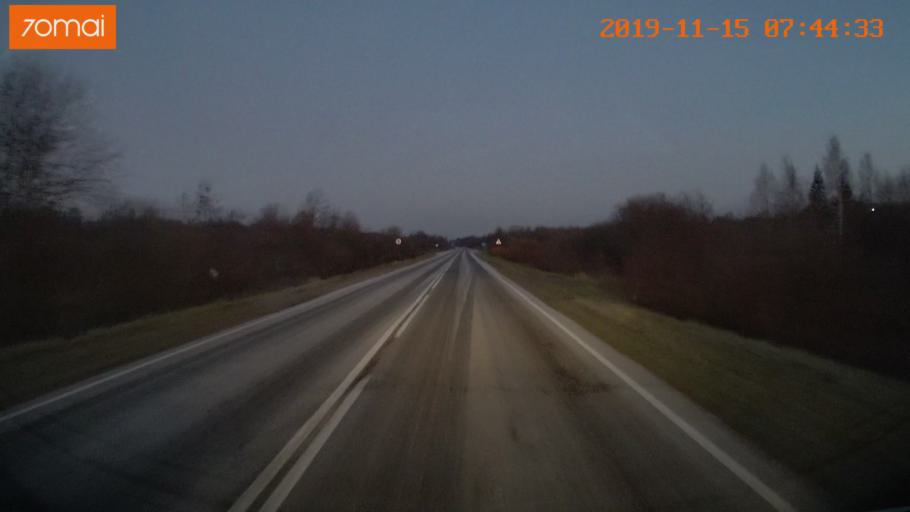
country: RU
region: Vologda
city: Sheksna
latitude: 58.8149
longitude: 38.3110
